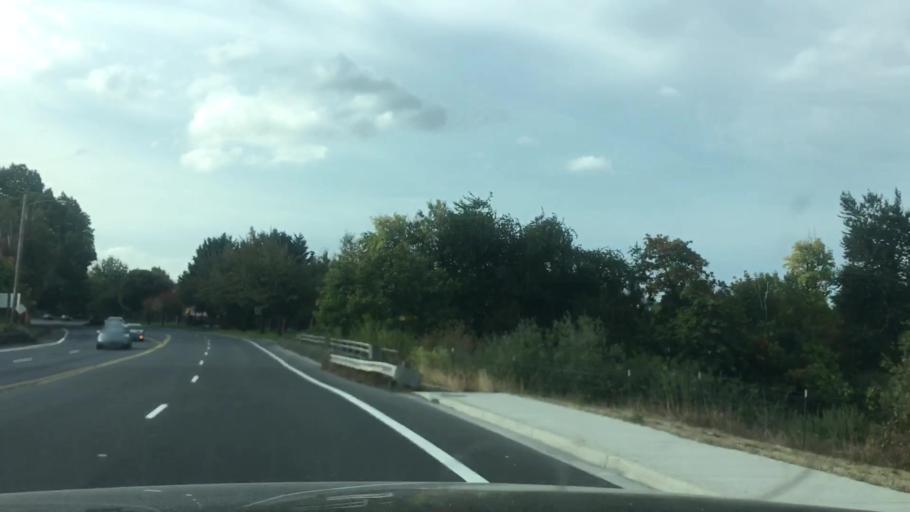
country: US
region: Oregon
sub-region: Lane County
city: Eugene
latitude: 44.0860
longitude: -123.1035
